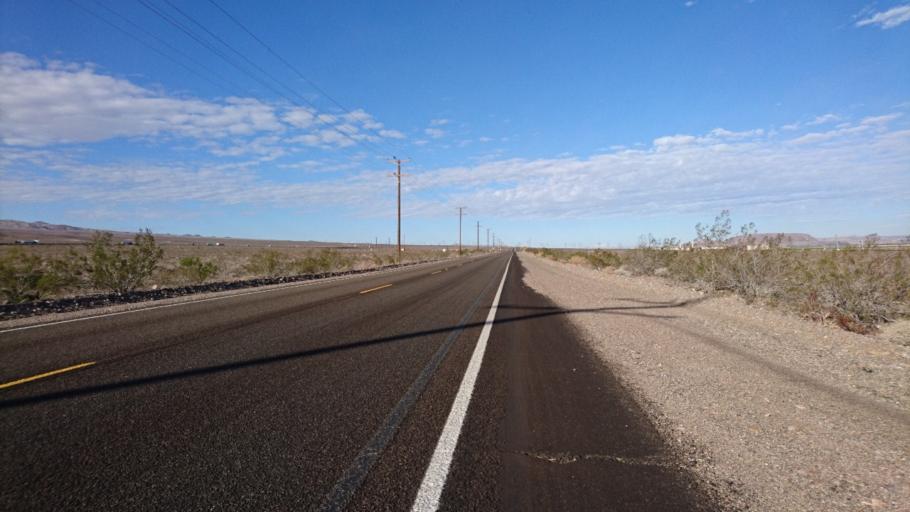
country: US
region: California
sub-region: San Bernardino County
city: Barstow
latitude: 34.8481
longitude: -116.7993
